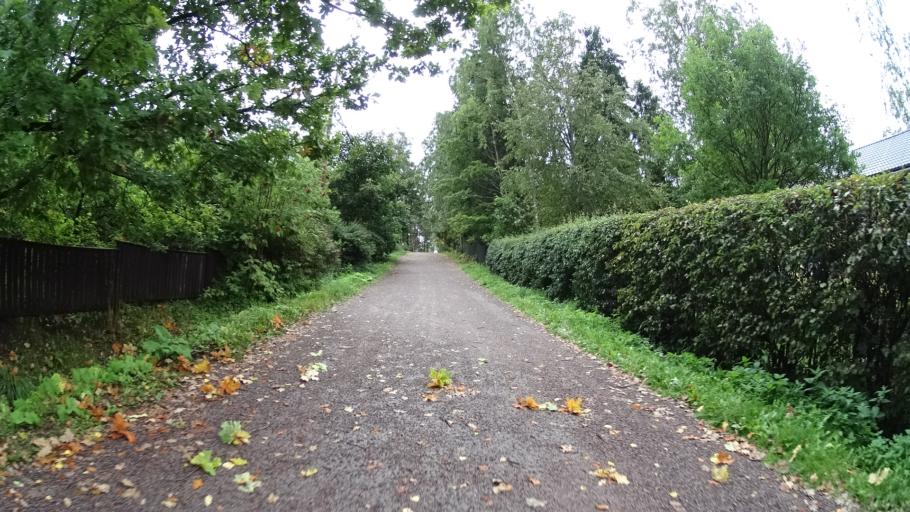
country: FI
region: Uusimaa
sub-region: Helsinki
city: Kilo
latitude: 60.2392
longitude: 24.7523
